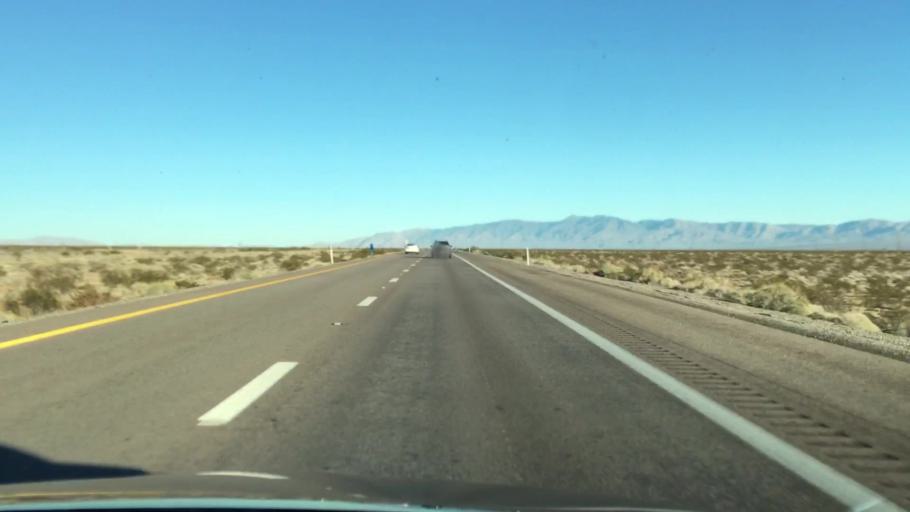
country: US
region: Nevada
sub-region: Clark County
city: Bunkerville
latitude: 36.7649
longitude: -114.3405
